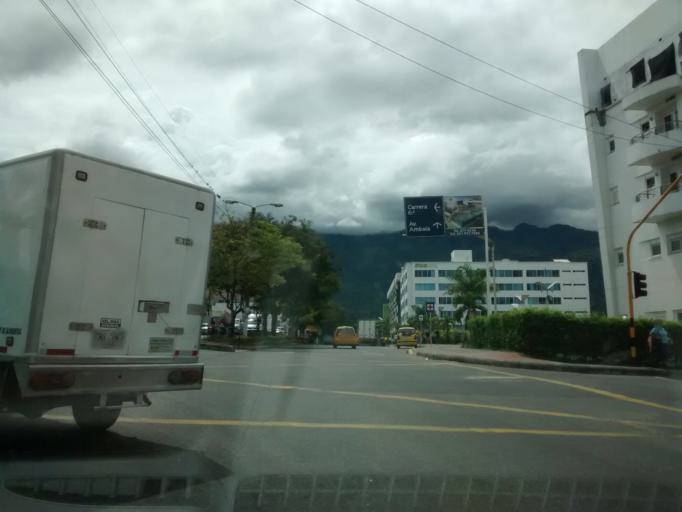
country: CO
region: Tolima
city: Ibague
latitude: 4.4366
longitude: -75.2031
